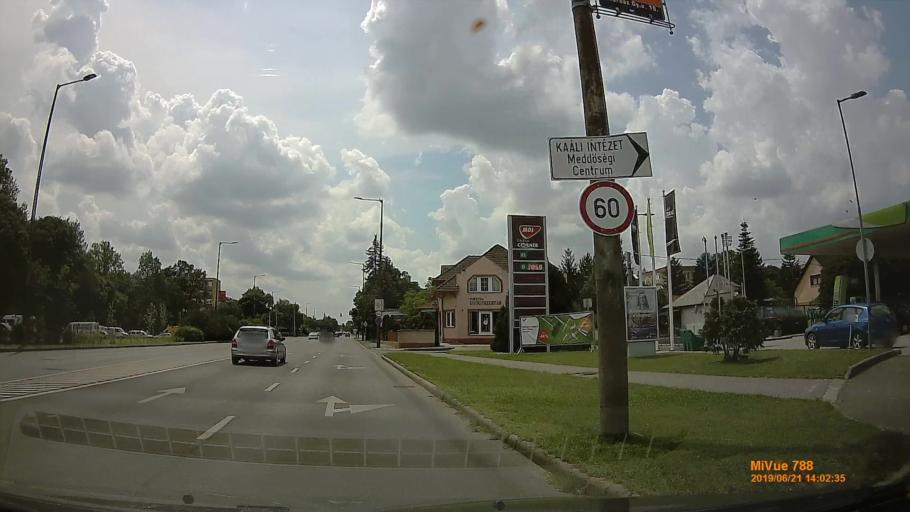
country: HU
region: Baranya
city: Pecs
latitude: 46.0681
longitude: 18.2002
